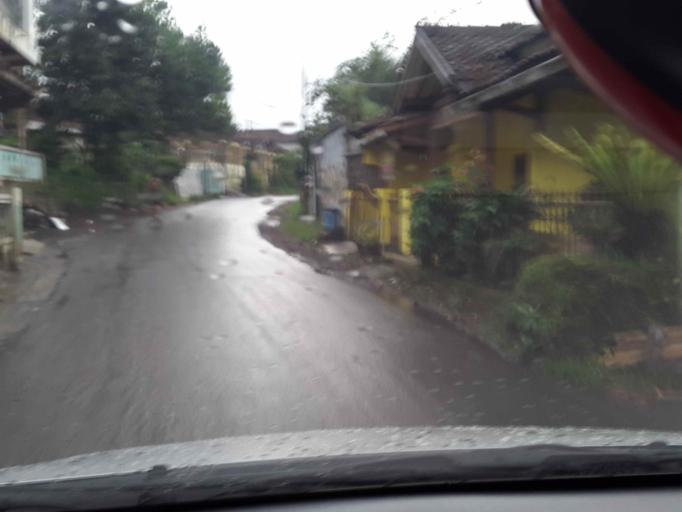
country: ID
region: West Java
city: Sukabumi
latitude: -6.9023
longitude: 106.8638
